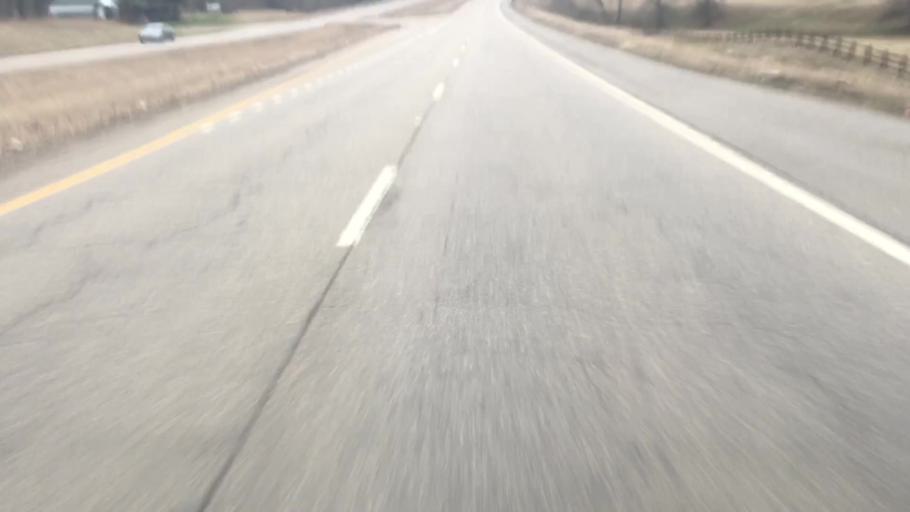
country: US
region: Alabama
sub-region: Walker County
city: Sumiton
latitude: 33.7943
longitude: -87.1022
